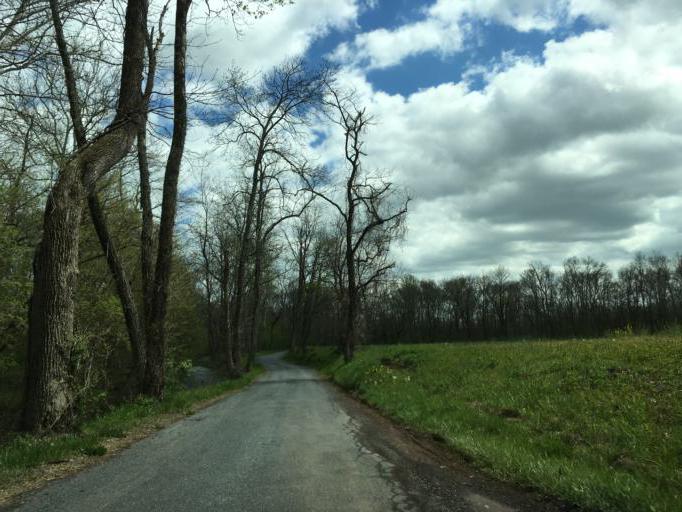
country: US
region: Maryland
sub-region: Frederick County
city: Thurmont
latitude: 39.5672
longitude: -77.3900
